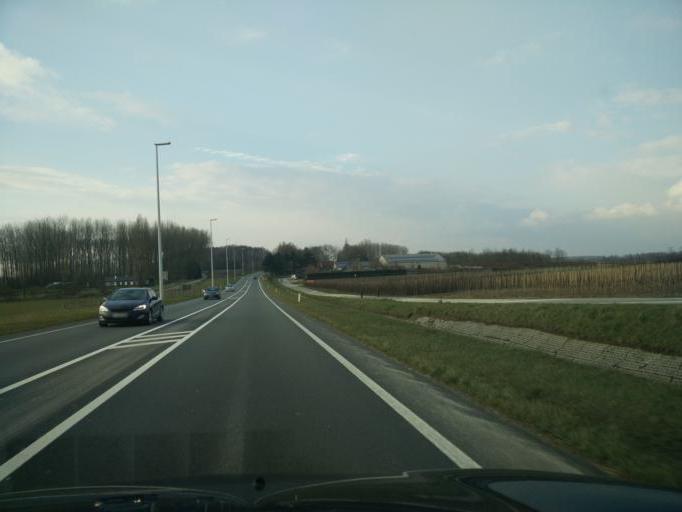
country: BE
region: Flanders
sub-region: Provincie Oost-Vlaanderen
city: Zottegem
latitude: 50.9082
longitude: 3.8216
